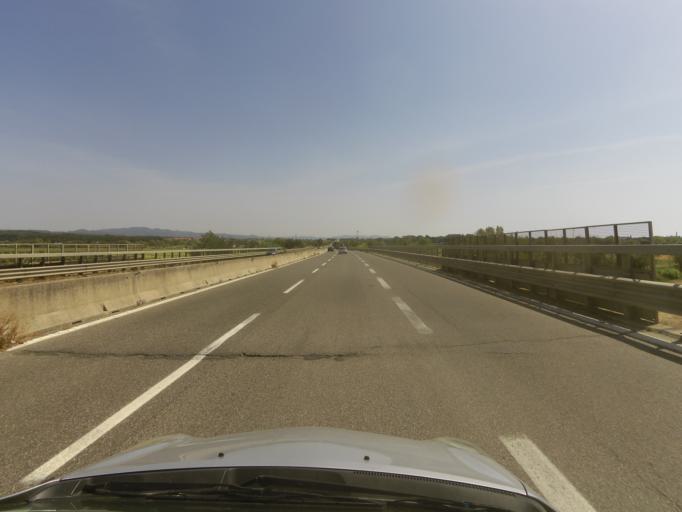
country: IT
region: Tuscany
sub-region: Provincia di Livorno
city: S.P. in Palazzi
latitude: 43.3297
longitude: 10.5270
